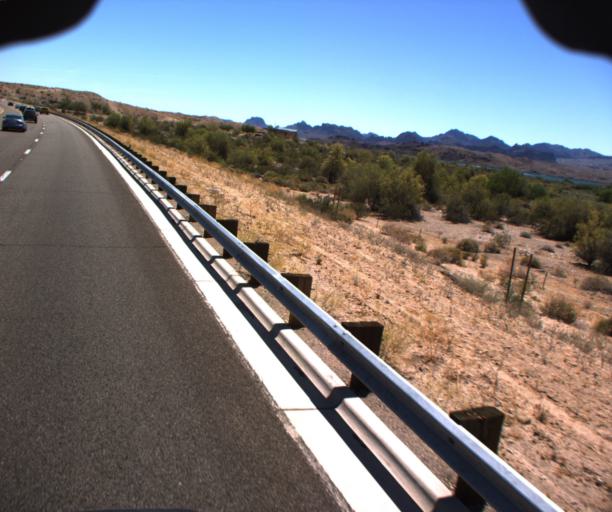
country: US
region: Arizona
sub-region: Mohave County
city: Lake Havasu City
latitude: 34.4548
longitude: -114.3268
